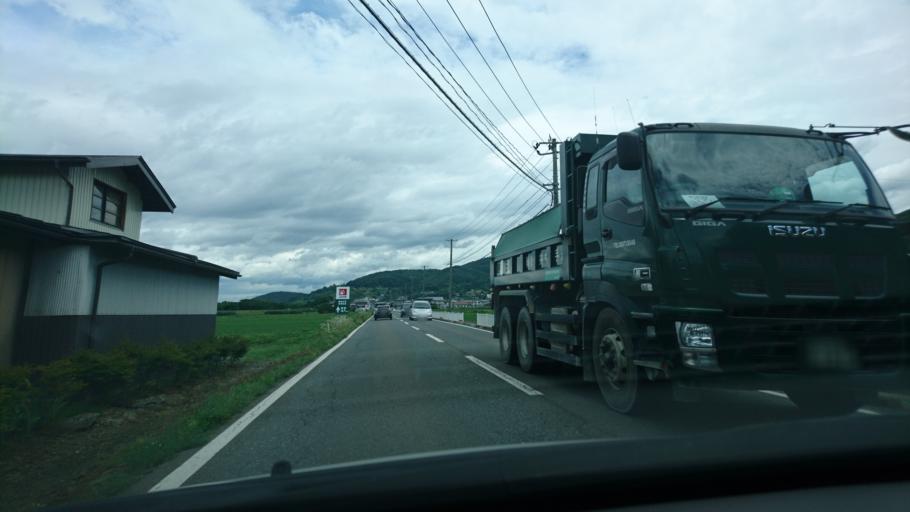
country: JP
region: Iwate
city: Morioka-shi
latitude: 39.6452
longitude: 141.1846
